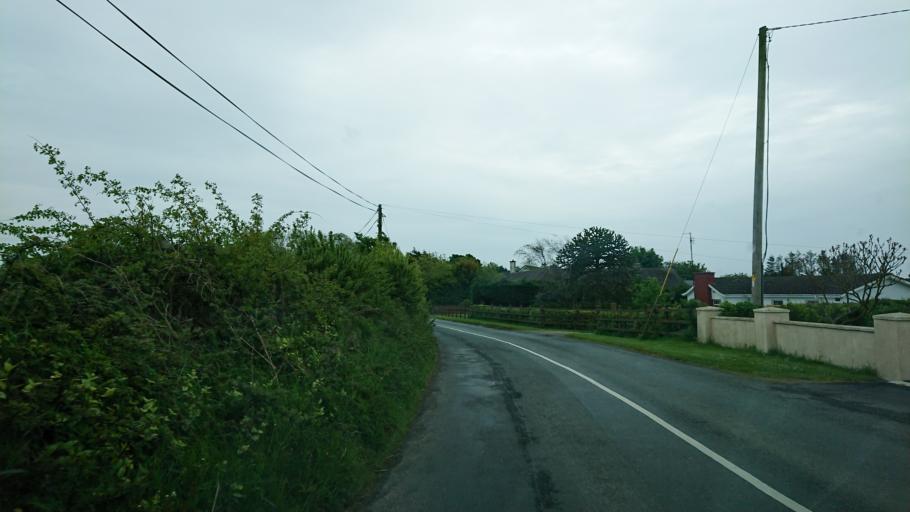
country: IE
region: Munster
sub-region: Waterford
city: Waterford
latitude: 52.2259
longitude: -7.0575
